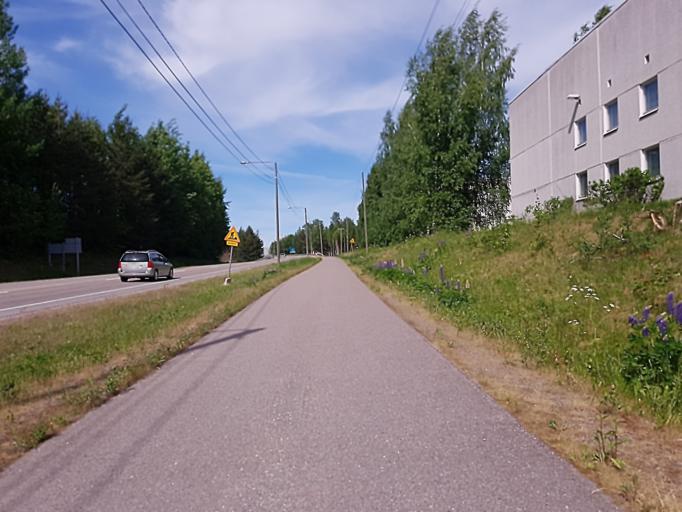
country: FI
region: Uusimaa
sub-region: Helsinki
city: Kilo
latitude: 60.3063
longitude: 24.8474
